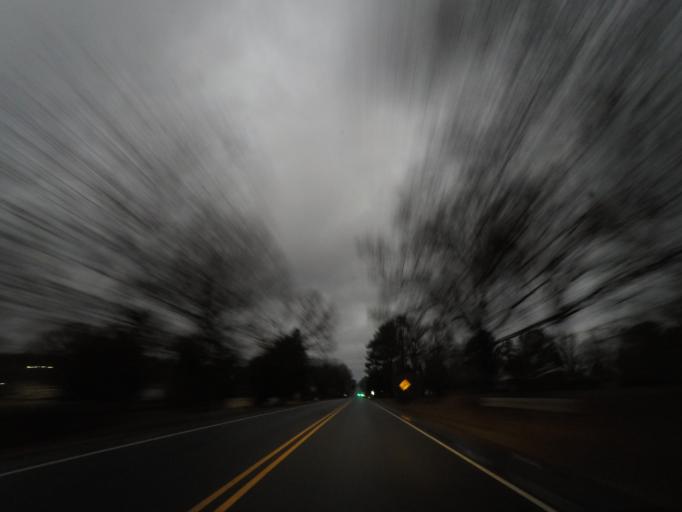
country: US
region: North Carolina
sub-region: Orange County
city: Hillsborough
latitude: 36.0886
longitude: -79.1031
